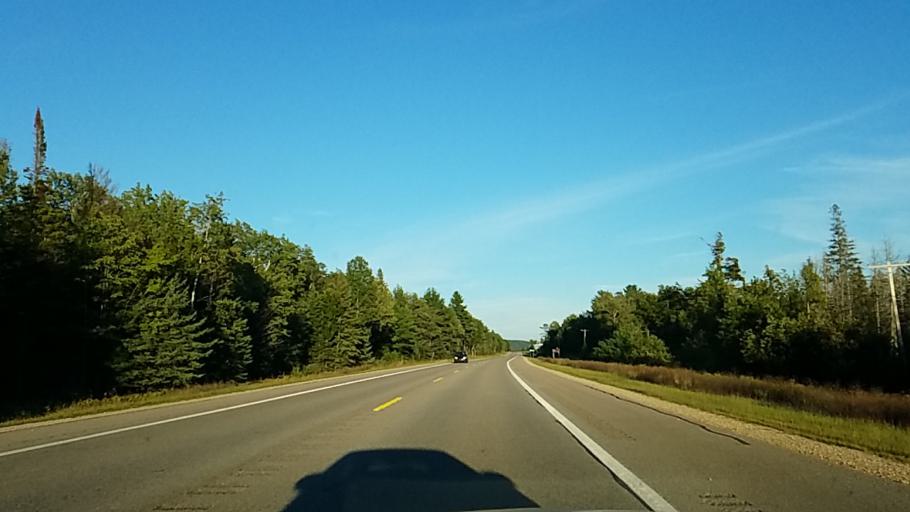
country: US
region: Michigan
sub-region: Alger County
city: Munising
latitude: 46.4419
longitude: -86.7296
